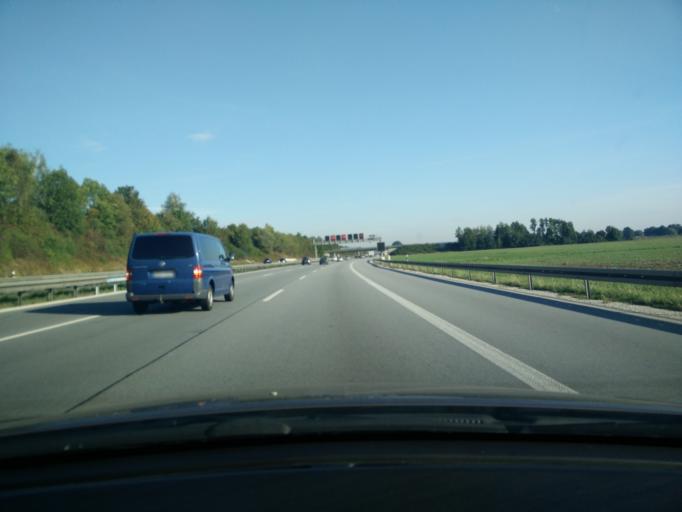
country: DE
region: Bavaria
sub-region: Upper Bavaria
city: Kranzberg
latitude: 48.4025
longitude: 11.5902
